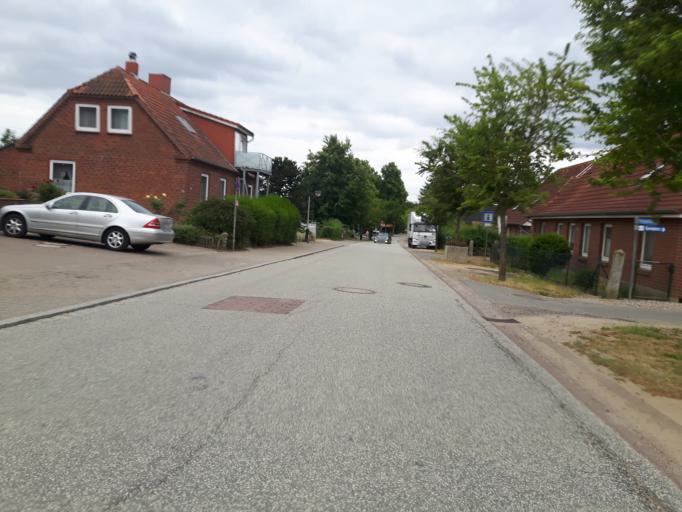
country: DE
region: Schleswig-Holstein
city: Schashagen
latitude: 54.1315
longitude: 10.9091
